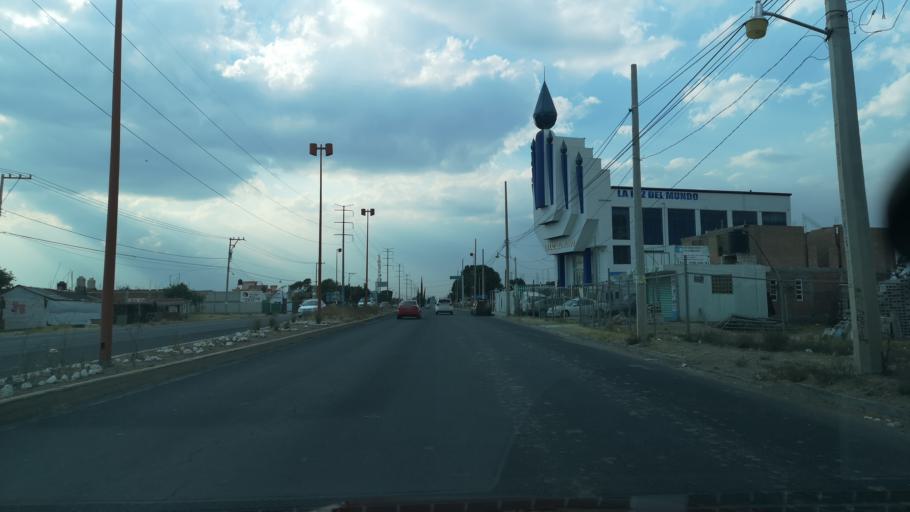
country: MX
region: Puebla
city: Cuanala
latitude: 19.0846
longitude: -98.3307
